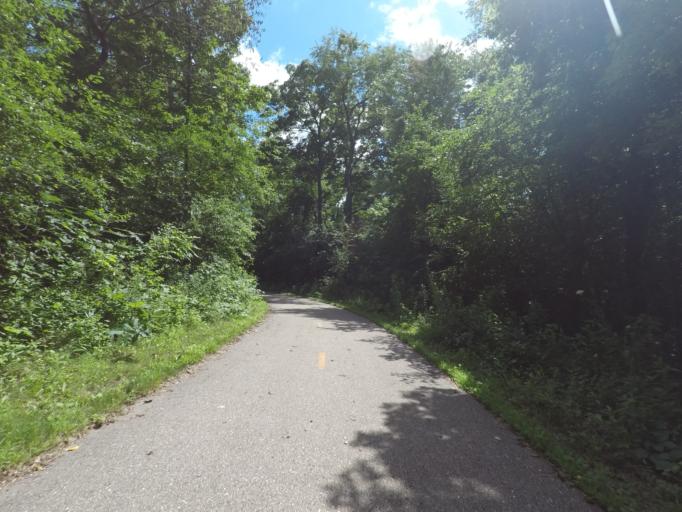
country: US
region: Wisconsin
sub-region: Dane County
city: Verona
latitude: 43.0172
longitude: -89.5240
